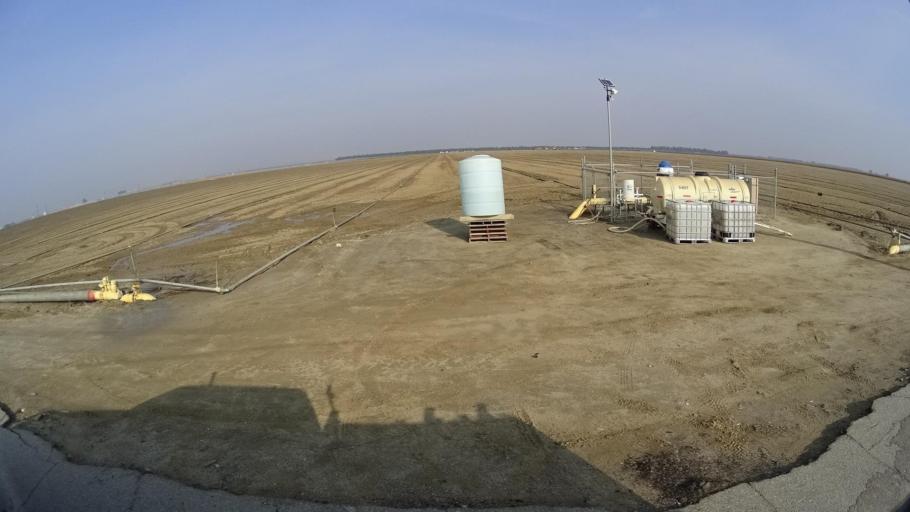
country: US
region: California
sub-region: Kern County
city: Weedpatch
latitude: 35.0934
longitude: -118.9631
